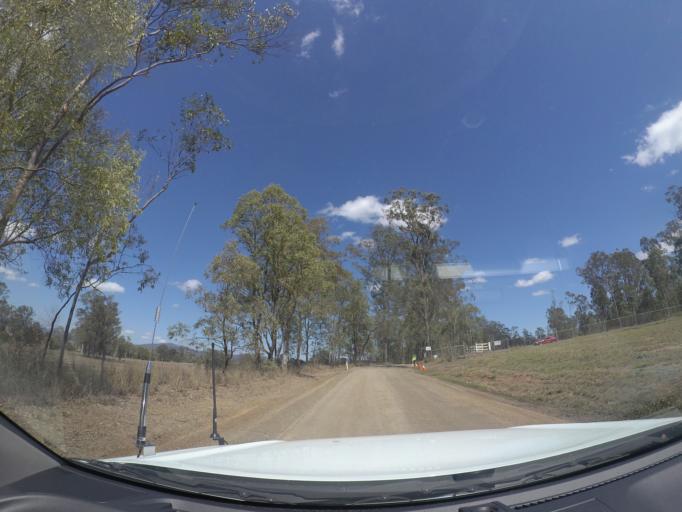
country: AU
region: Queensland
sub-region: Logan
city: Cedar Vale
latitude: -27.8386
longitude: 152.9303
